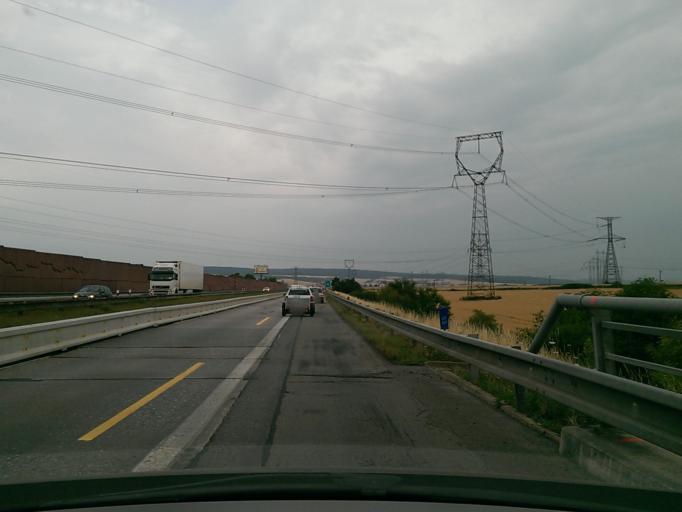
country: CZ
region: South Moravian
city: Ricany
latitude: 49.2049
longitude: 16.4201
